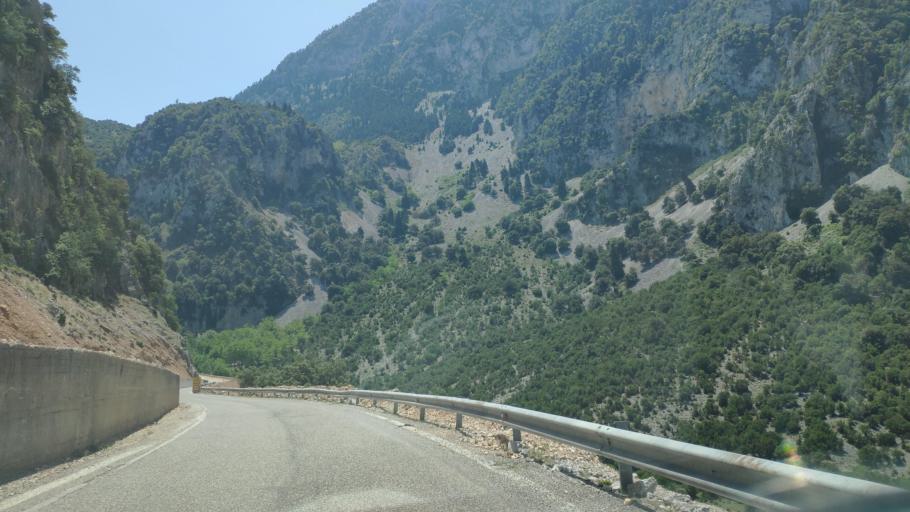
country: GR
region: West Greece
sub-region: Nomos Aitolias kai Akarnanias
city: Krikellos
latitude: 39.0077
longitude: 21.3675
